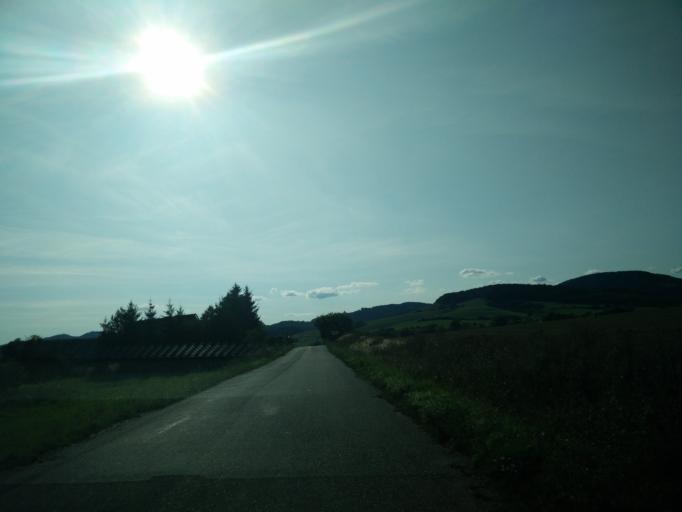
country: SK
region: Nitriansky
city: Handlova
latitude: 48.8899
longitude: 18.7680
